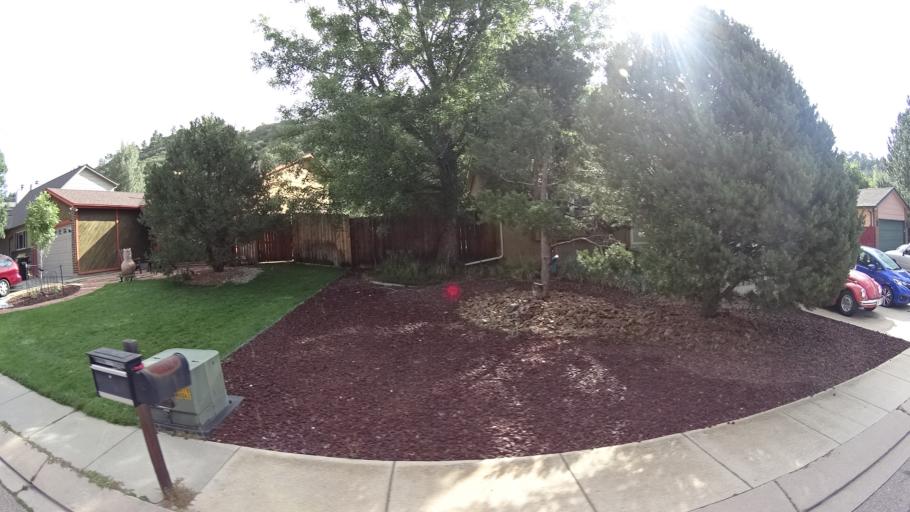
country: US
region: Colorado
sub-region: El Paso County
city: Air Force Academy
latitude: 38.9151
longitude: -104.8596
